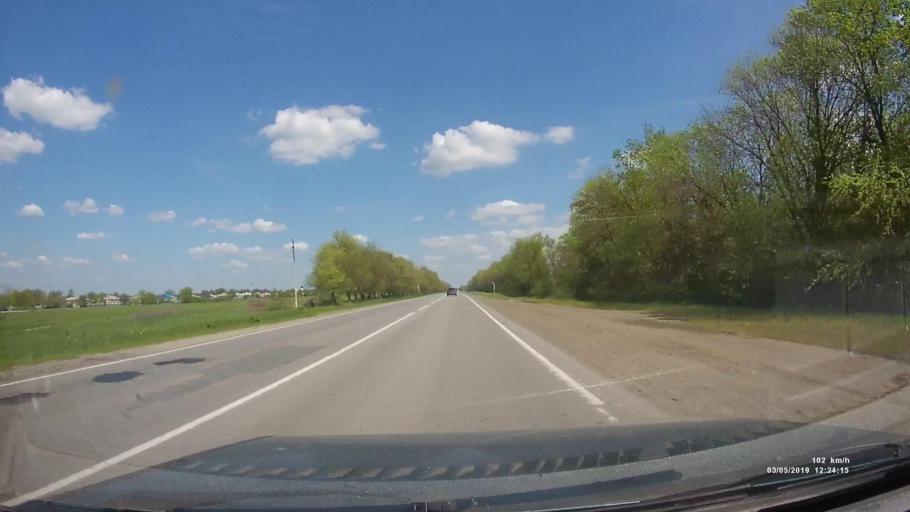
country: RU
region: Rostov
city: Semikarakorsk
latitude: 47.4179
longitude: 40.6963
